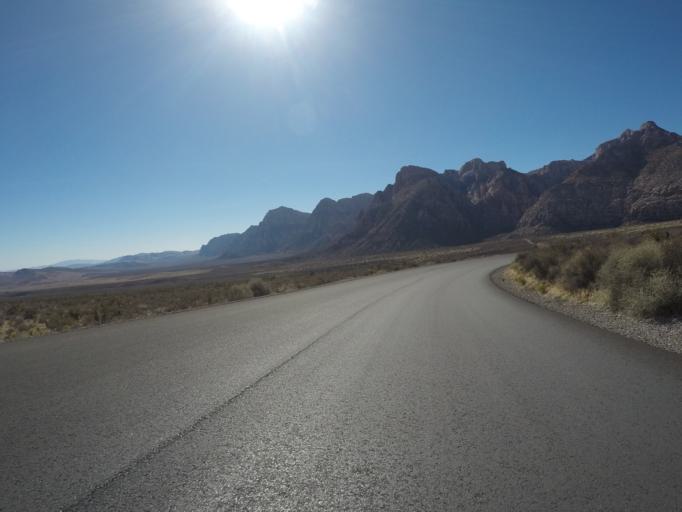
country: US
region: Nevada
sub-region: Clark County
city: Summerlin South
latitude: 36.1633
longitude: -115.4759
